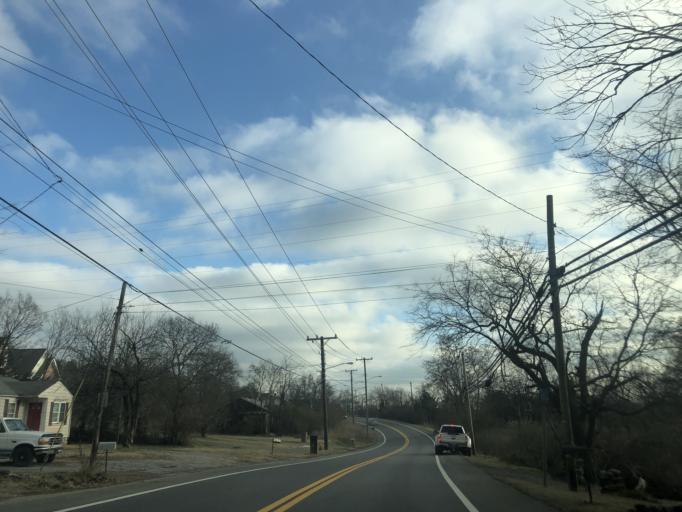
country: US
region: Tennessee
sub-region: Davidson County
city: Nashville
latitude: 36.2106
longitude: -86.7967
